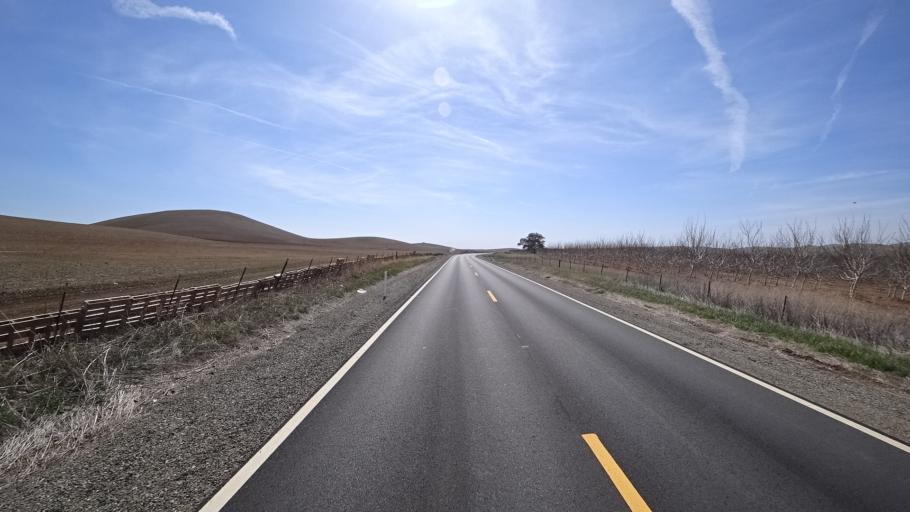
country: US
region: California
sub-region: Glenn County
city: Willows
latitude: 39.5446
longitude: -122.3485
